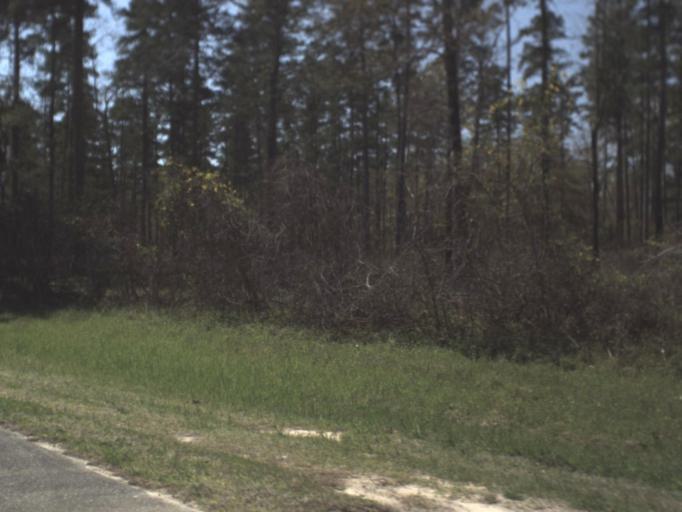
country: US
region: Florida
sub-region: Jefferson County
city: Monticello
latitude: 30.3859
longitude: -84.0090
